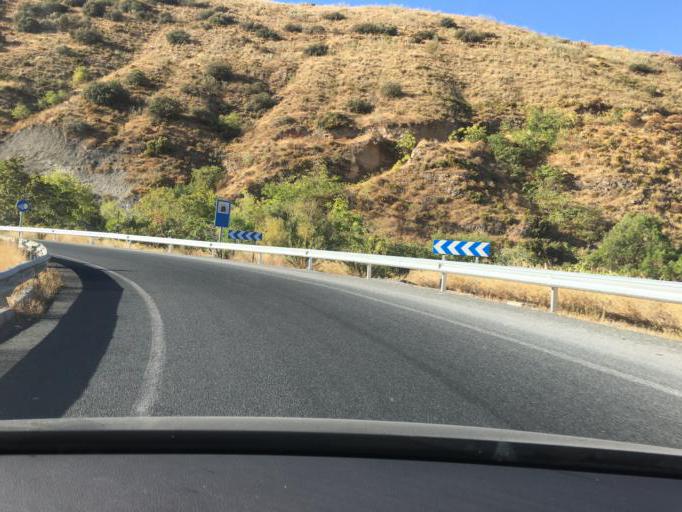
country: ES
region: Andalusia
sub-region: Provincia de Granada
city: Huetor Vega
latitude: 37.1618
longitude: -3.5727
